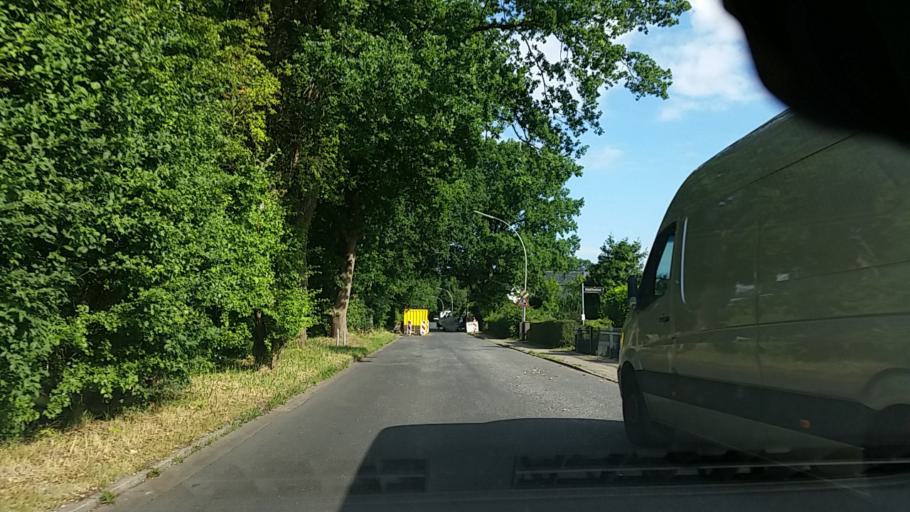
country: DE
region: Hamburg
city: Hummelsbuettel
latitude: 53.6706
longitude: 10.0568
